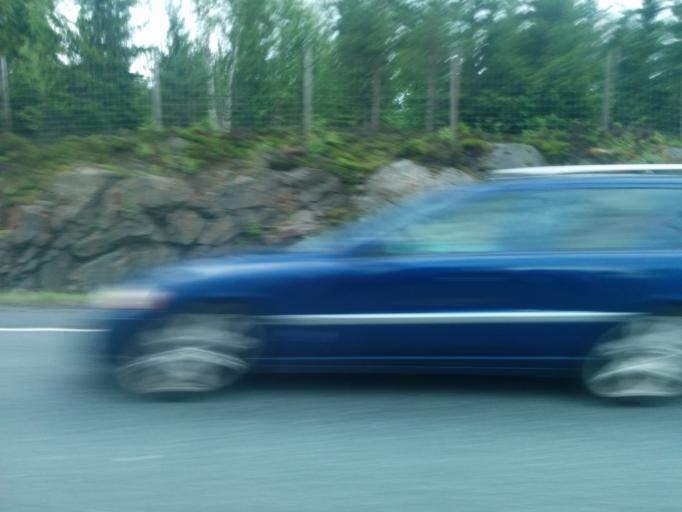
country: FI
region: Pirkanmaa
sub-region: Tampere
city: Orivesi
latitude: 61.6643
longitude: 24.2675
